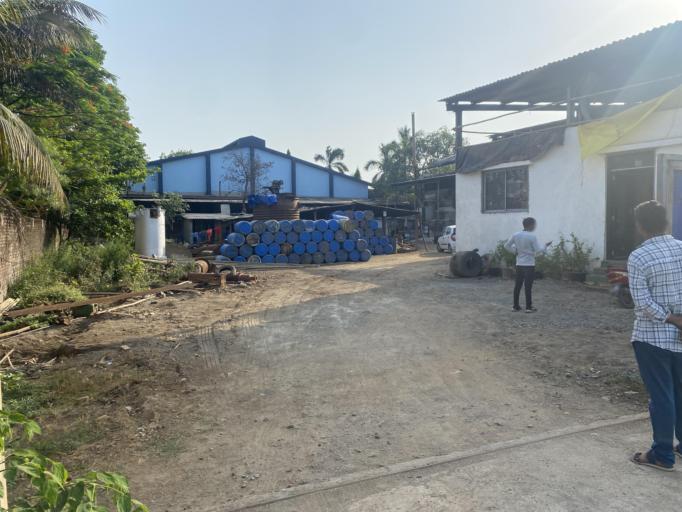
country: IN
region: Gujarat
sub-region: Valsad
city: Vapi
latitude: 20.3029
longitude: 72.8490
